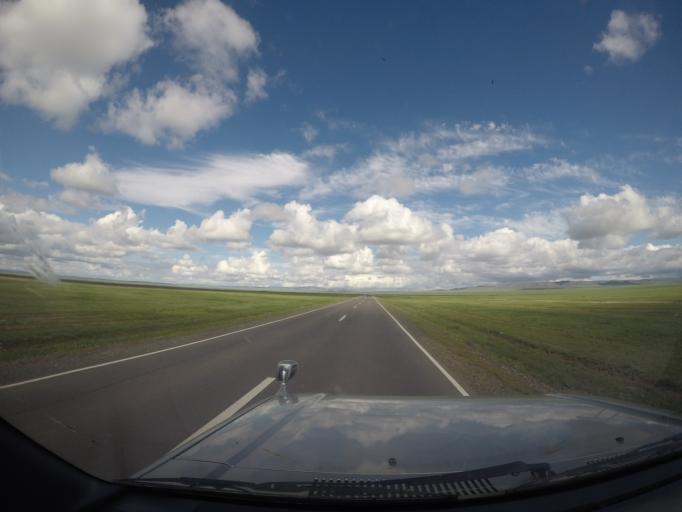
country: MN
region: Hentiy
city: Moron
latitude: 47.4198
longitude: 110.0016
